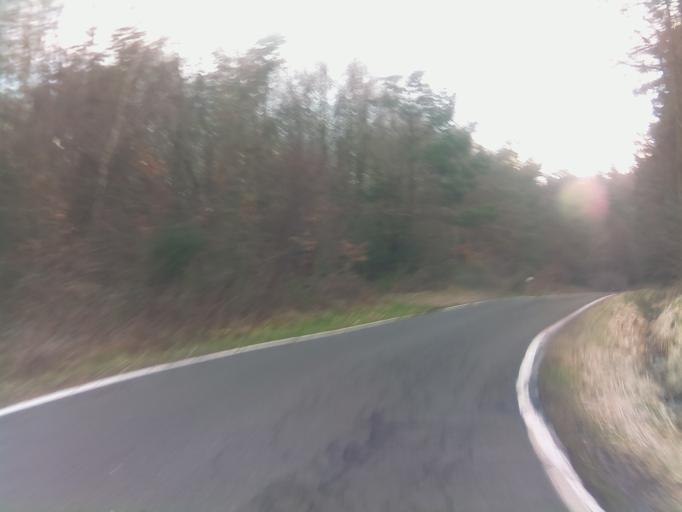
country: DE
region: Rheinland-Pfalz
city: Oberheimbach
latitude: 49.9844
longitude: 7.8024
